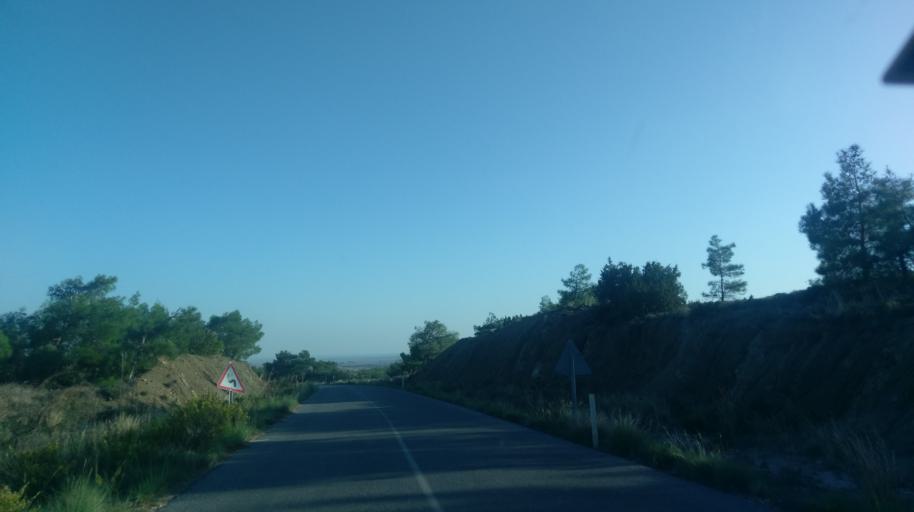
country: CY
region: Ammochostos
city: Lefkonoiko
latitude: 35.2973
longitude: 33.6434
